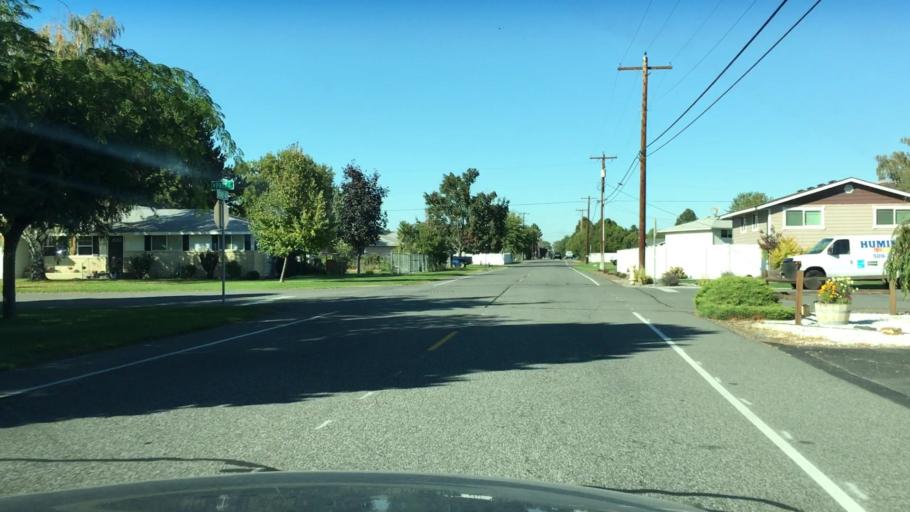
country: US
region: Washington
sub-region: Benton County
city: Kennewick
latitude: 46.2358
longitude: -119.1437
